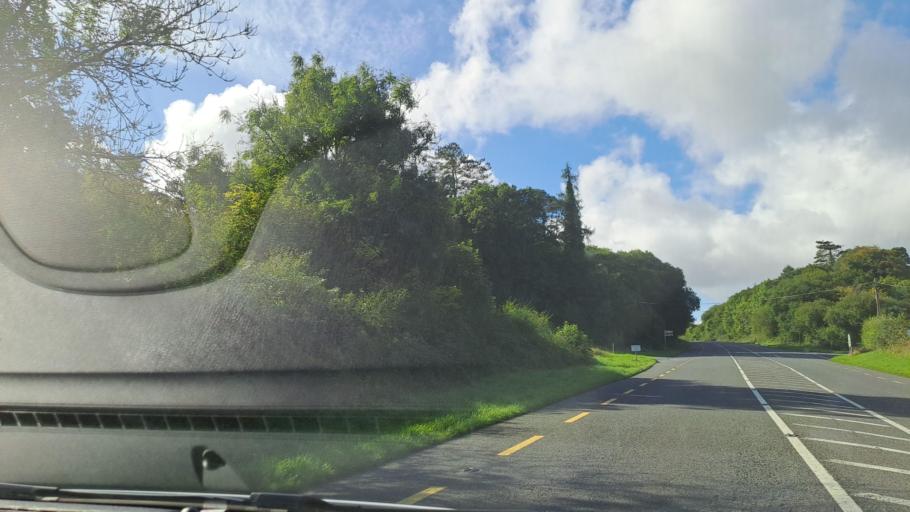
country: IE
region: Ulster
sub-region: County Monaghan
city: Carrickmacross
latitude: 53.9474
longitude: -6.7641
